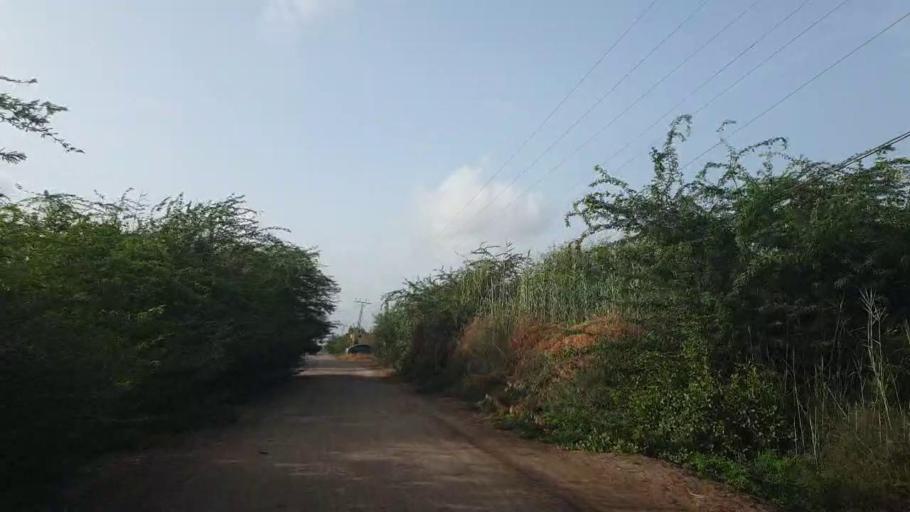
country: PK
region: Sindh
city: Tando Bago
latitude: 24.6446
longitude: 69.1117
